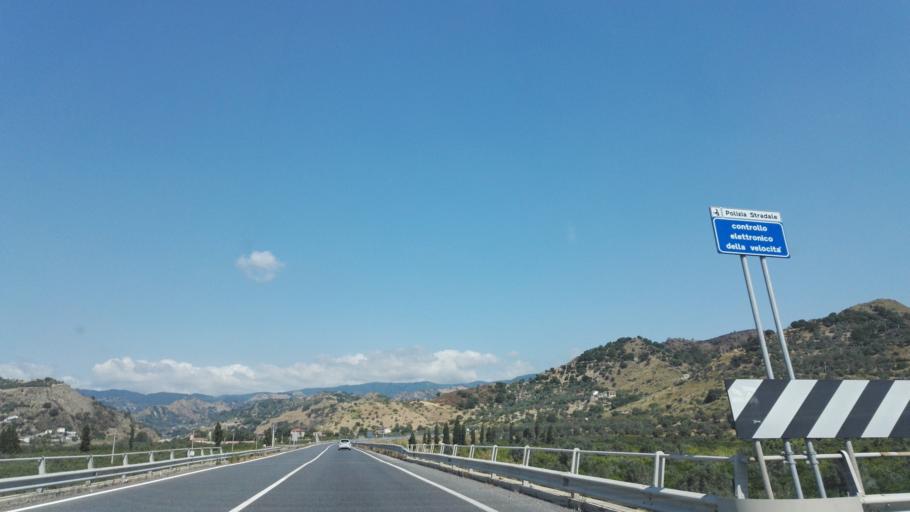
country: IT
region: Calabria
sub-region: Provincia di Reggio Calabria
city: Gioiosa Ionica
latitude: 38.3252
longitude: 16.2943
